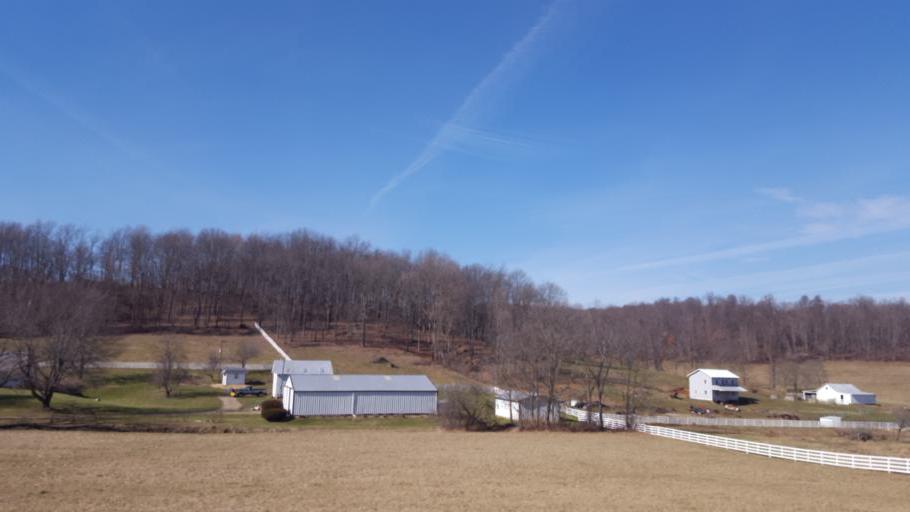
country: US
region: Ohio
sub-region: Sandusky County
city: Bellville
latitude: 40.5531
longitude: -82.3926
